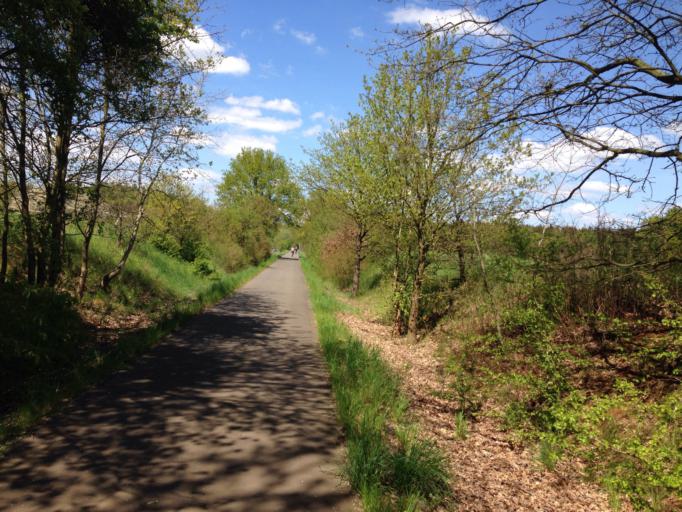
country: DE
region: Hesse
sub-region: Regierungsbezirk Giessen
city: Hungen
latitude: 50.5110
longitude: 8.9322
